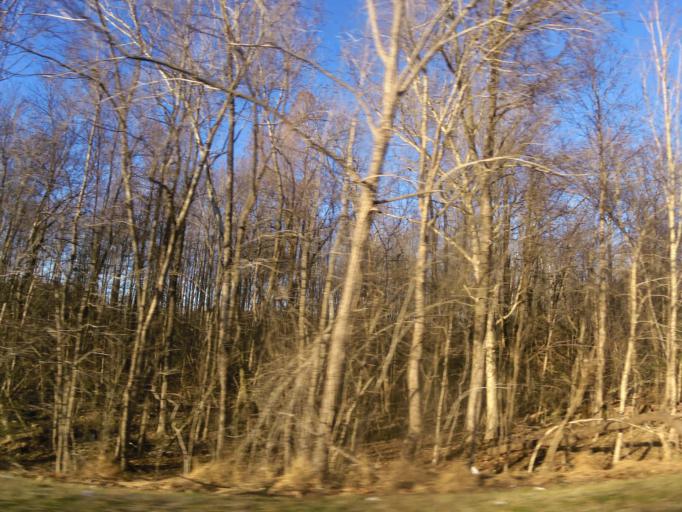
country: US
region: Virginia
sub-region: City of Franklin
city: Franklin
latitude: 36.6502
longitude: -76.8560
